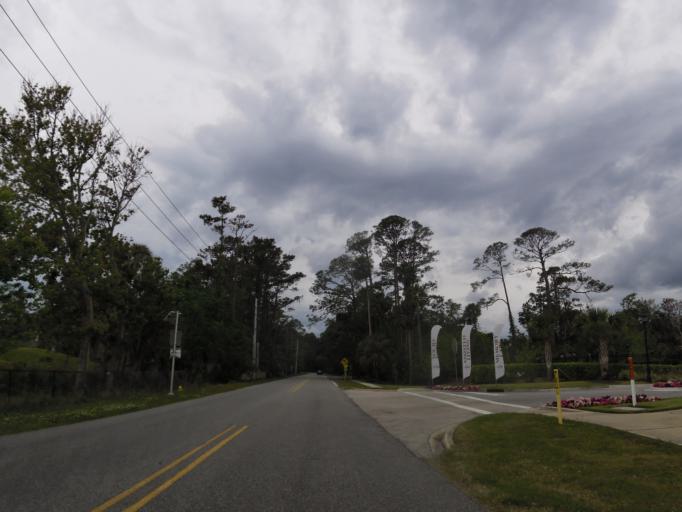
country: US
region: Florida
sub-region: Saint Johns County
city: Ponte Vedra Beach
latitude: 30.2273
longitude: -81.3916
